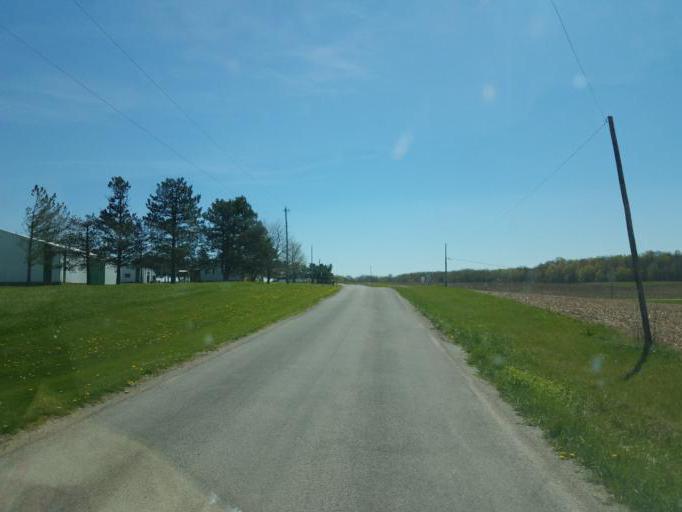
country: US
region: Ohio
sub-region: Morrow County
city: Mount Gilead
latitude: 40.5981
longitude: -82.7912
